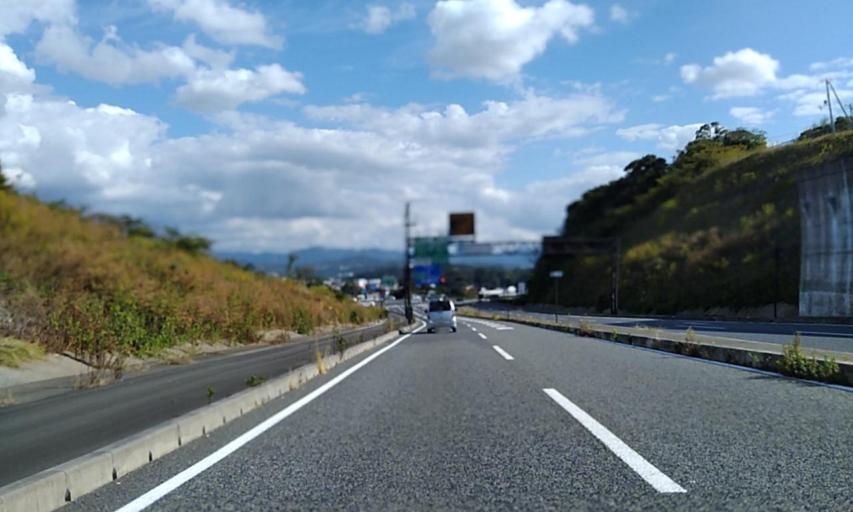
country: JP
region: Wakayama
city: Tanabe
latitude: 33.7467
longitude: 135.3666
